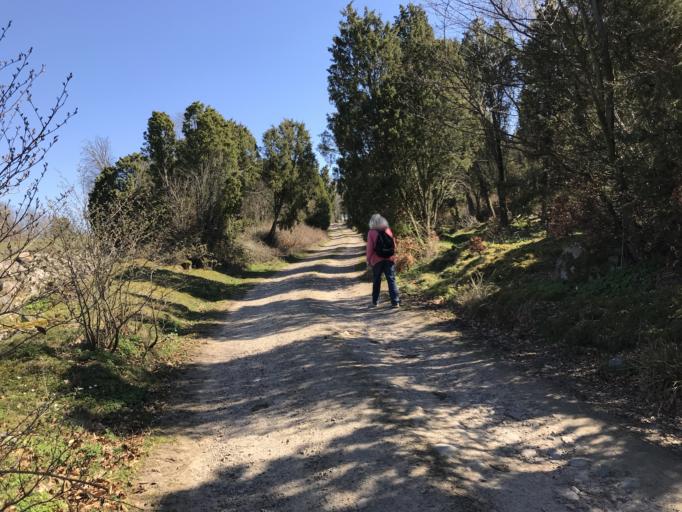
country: SE
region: Skane
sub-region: Eslovs Kommun
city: Stehag
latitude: 56.0107
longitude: 13.3724
